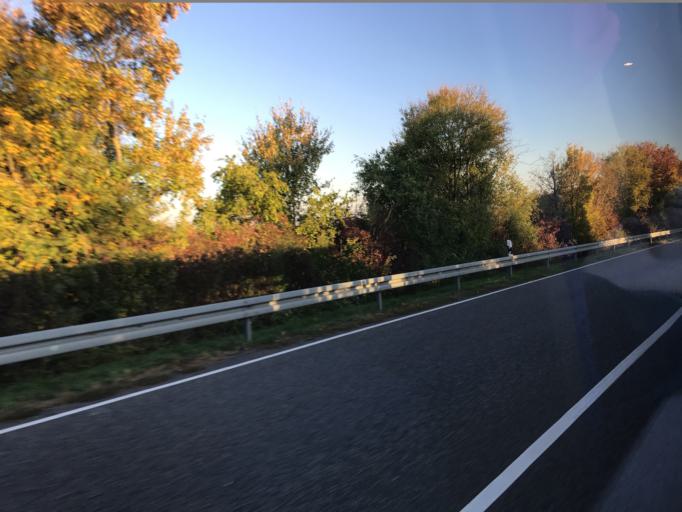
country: DE
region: Hesse
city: Kelkheim (Taunus)
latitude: 50.1303
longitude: 8.4720
